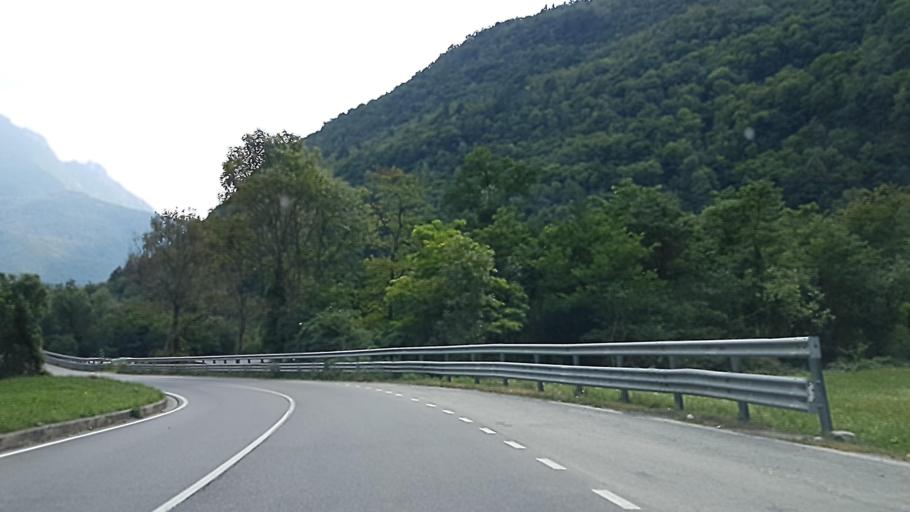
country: IT
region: Lombardy
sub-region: Provincia di Sondrio
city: San Giacomo Filippo
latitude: 46.3271
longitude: 9.3758
